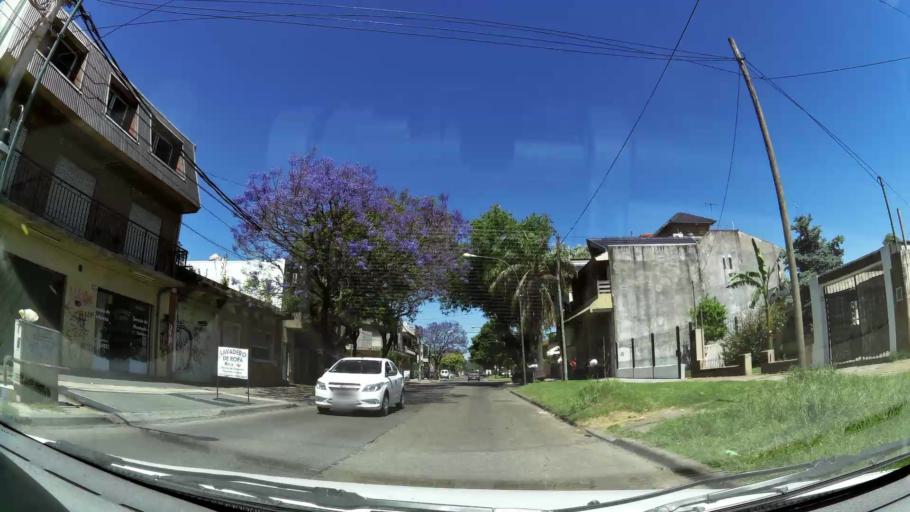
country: AR
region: Buenos Aires
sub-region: Partido de Vicente Lopez
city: Olivos
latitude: -34.5164
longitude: -58.5342
